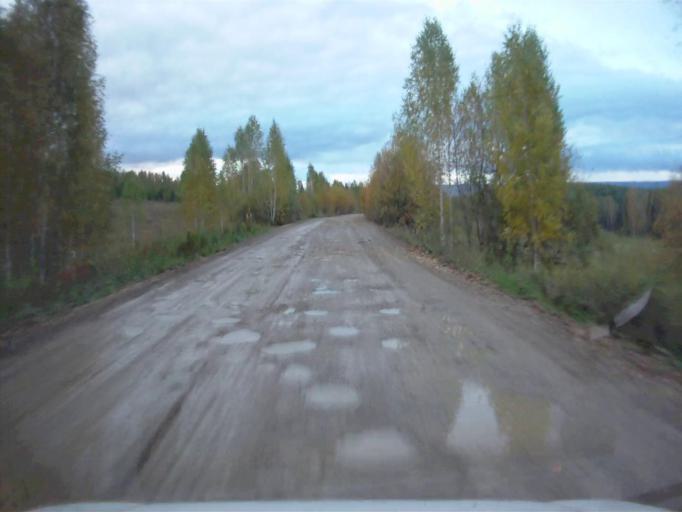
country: RU
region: Sverdlovsk
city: Mikhaylovsk
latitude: 56.2064
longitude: 59.2051
